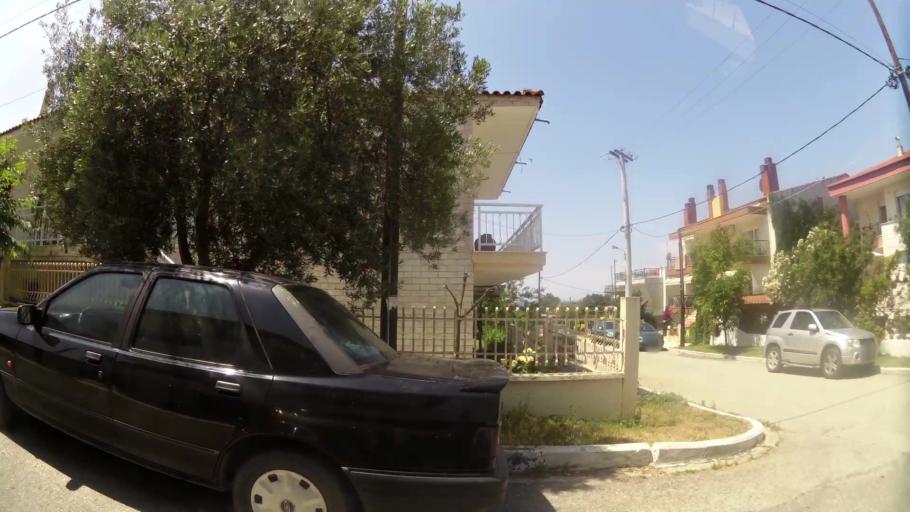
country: GR
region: Central Macedonia
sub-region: Nomos Thessalonikis
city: Nea Michaniona
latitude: 40.4749
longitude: 22.8671
